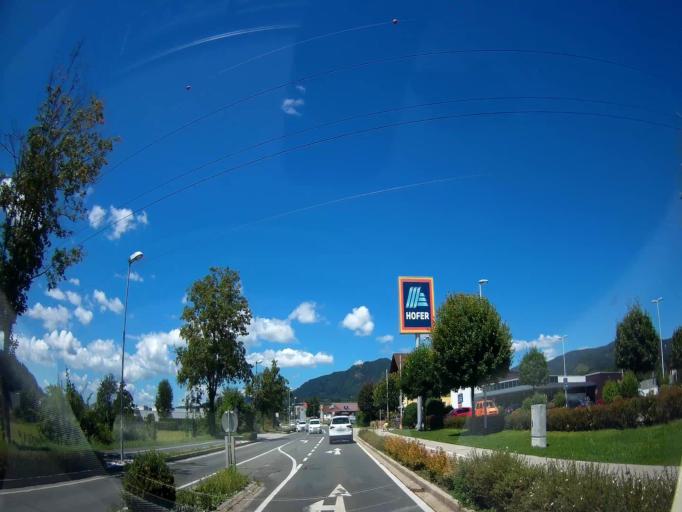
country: AT
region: Carinthia
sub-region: Politischer Bezirk Sankt Veit an der Glan
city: Sankt Veit an der Glan
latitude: 46.7662
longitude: 14.3753
